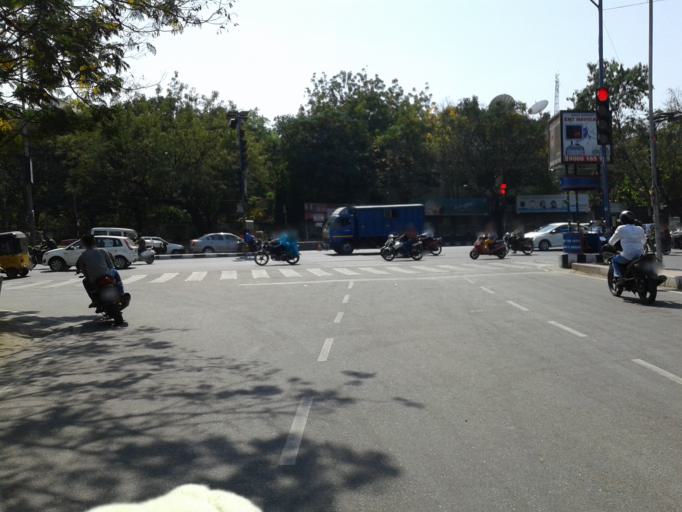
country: IN
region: Telangana
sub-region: Hyderabad
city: Hyderabad
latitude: 17.4275
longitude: 78.4396
